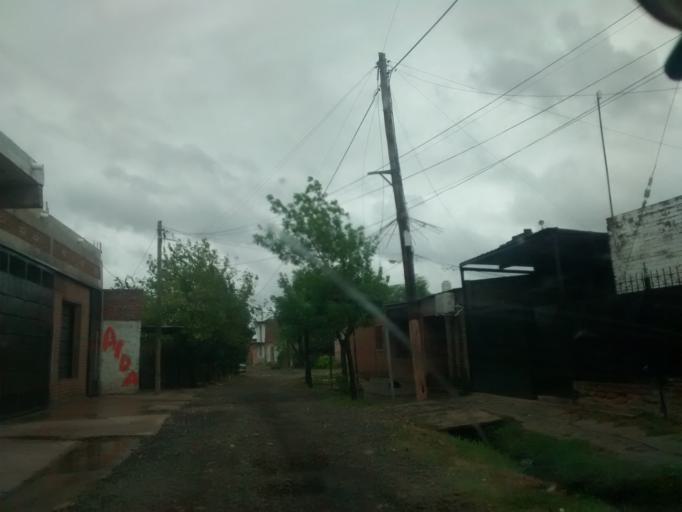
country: AR
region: Chaco
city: Resistencia
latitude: -27.4385
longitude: -58.9772
